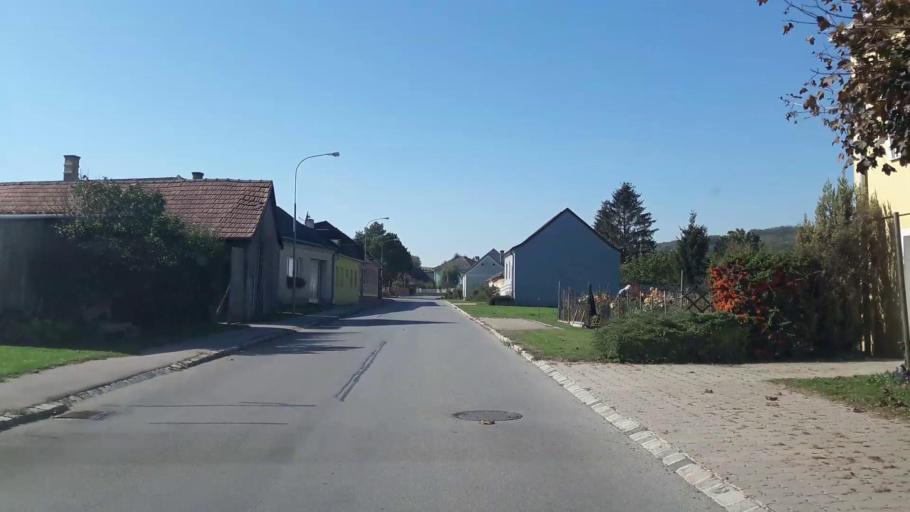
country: AT
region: Lower Austria
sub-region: Politischer Bezirk Korneuburg
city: Grossrussbach
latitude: 48.4788
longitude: 16.3807
